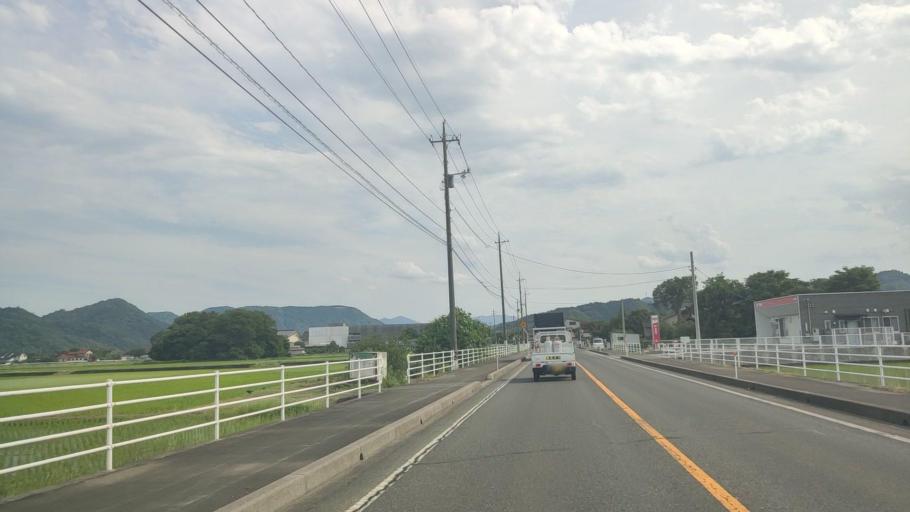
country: JP
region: Tottori
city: Tottori
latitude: 35.4578
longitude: 134.2034
